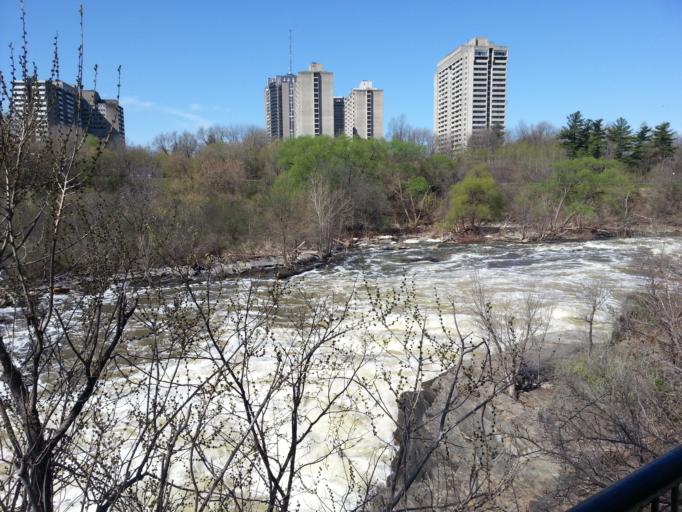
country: CA
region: Ontario
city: Ottawa
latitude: 45.3717
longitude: -75.6977
